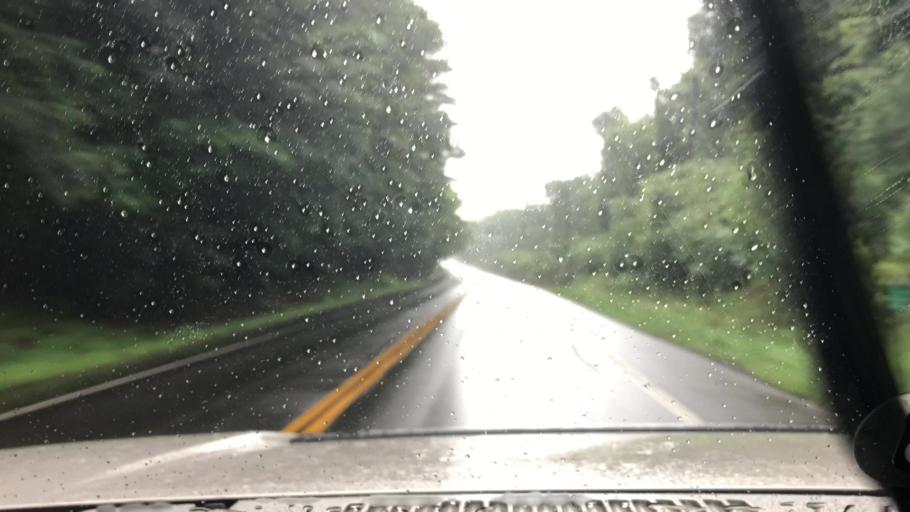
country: US
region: New York
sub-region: Greene County
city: Palenville
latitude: 42.2156
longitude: -73.9861
